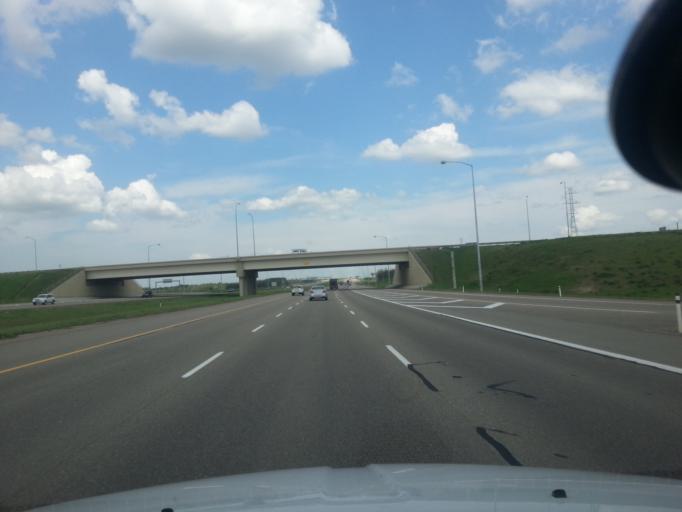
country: CA
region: Alberta
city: St. Albert
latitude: 53.5901
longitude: -113.6479
